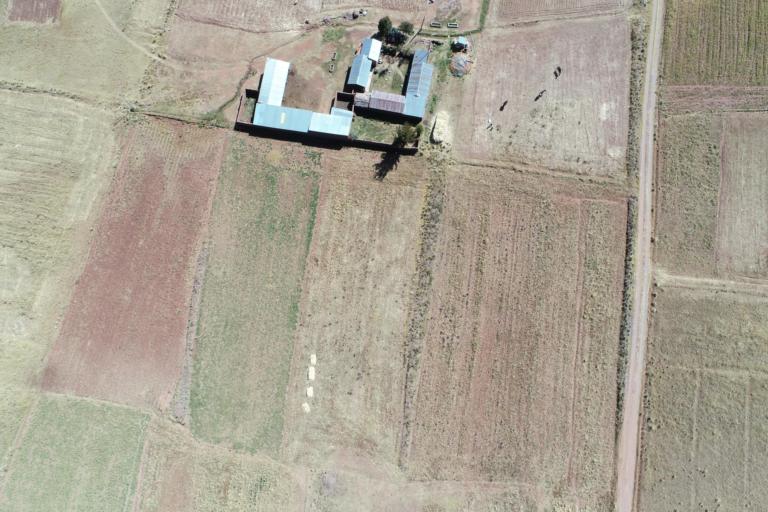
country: BO
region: La Paz
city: Tiahuanaco
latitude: -16.5994
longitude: -68.7822
